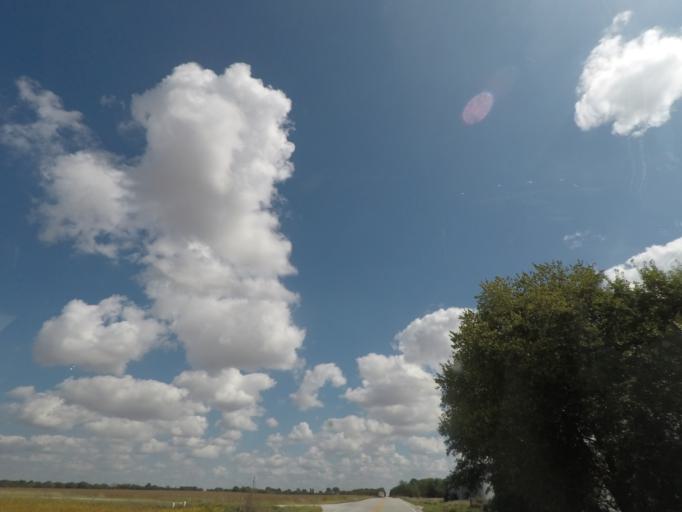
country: US
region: Iowa
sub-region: Story County
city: Nevada
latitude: 42.0778
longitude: -93.3675
